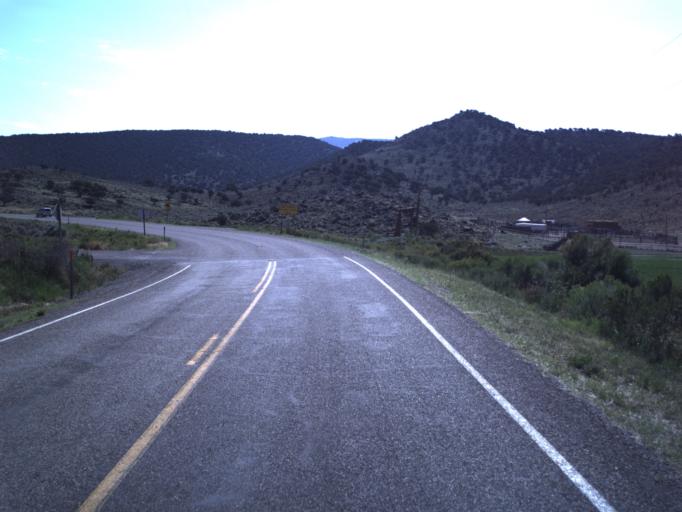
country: US
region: Utah
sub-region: Wayne County
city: Loa
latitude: 38.4694
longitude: -111.5794
